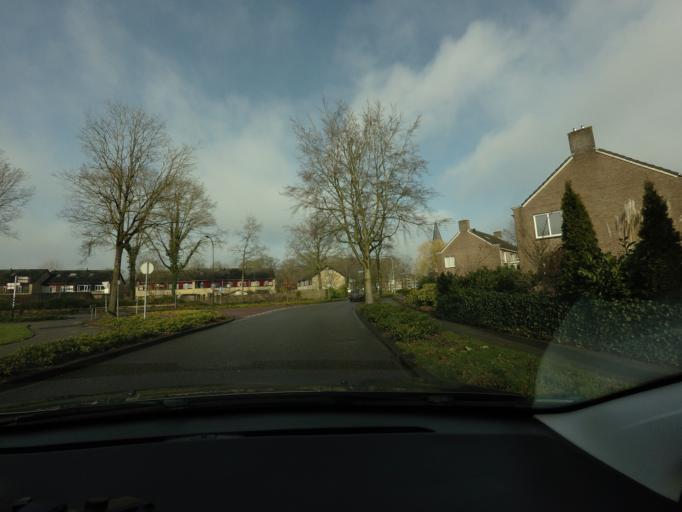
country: NL
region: Drenthe
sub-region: Gemeente Hoogeveen
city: Hoogeveen
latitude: 52.8566
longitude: 6.5173
